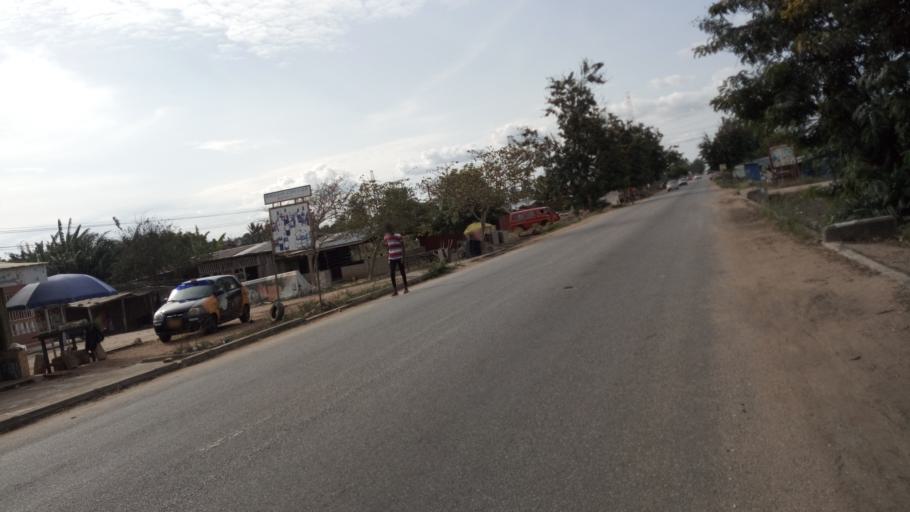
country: GH
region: Central
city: Winneba
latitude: 5.3864
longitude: -0.6441
